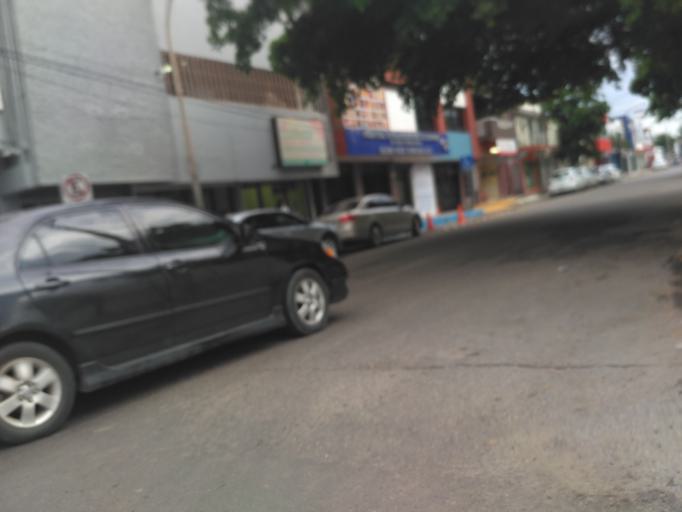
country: MX
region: Sinaloa
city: Culiacan
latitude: 24.8038
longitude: -107.3932
